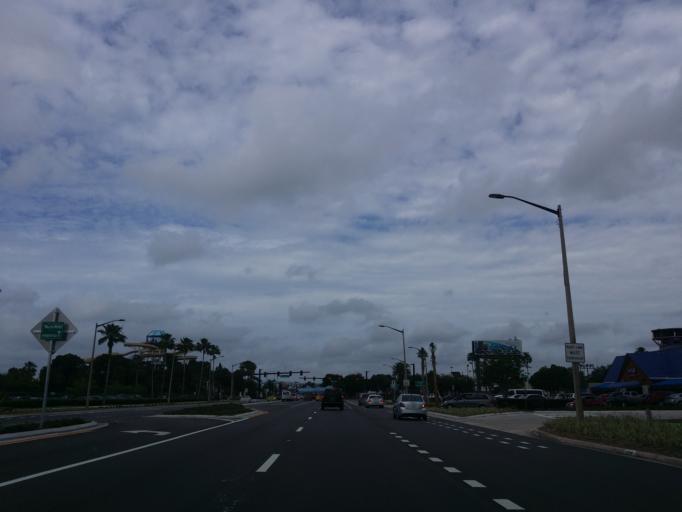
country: US
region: Florida
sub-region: Orange County
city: Tangelo Park
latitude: 28.4624
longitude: -81.4620
